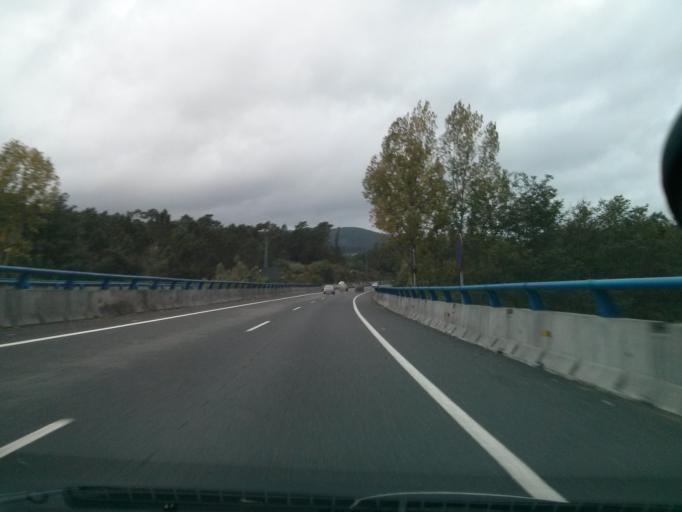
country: ES
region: Galicia
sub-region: Provincia de Pontevedra
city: Ponteareas
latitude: 42.1540
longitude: -8.5136
